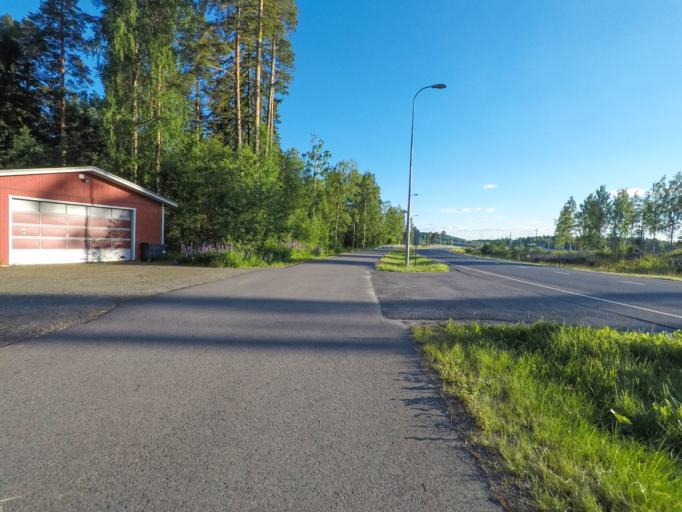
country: FI
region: Northern Savo
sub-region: Kuopio
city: Kuopio
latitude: 62.9552
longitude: 27.6892
